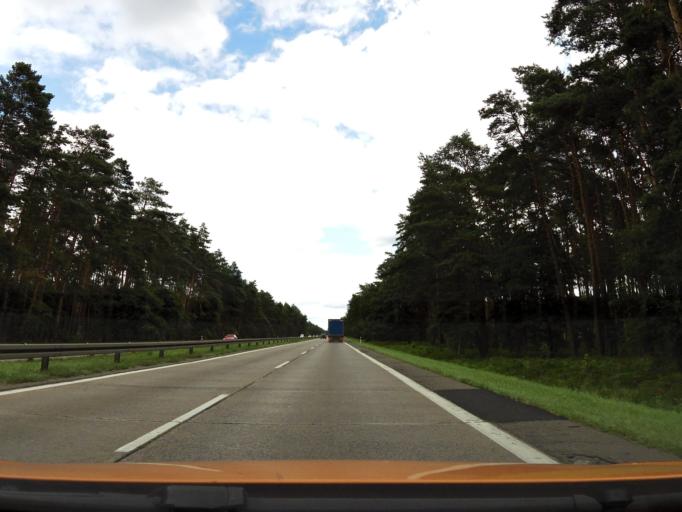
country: PL
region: West Pomeranian Voivodeship
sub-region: Powiat stargardzki
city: Kobylanka
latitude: 53.4170
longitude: 14.7497
